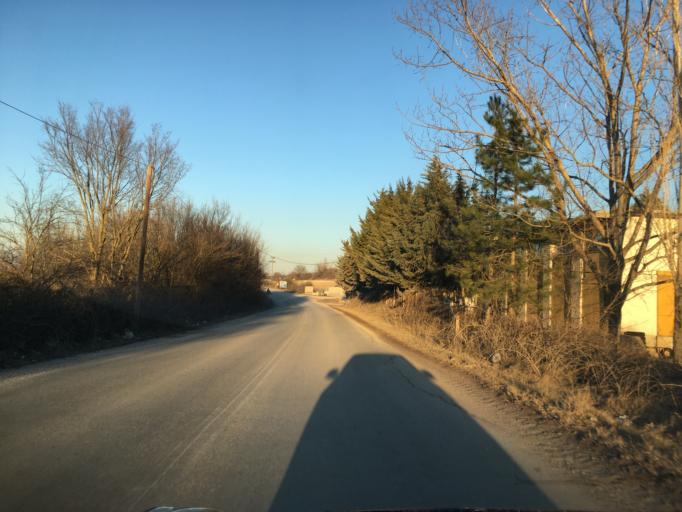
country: GR
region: West Macedonia
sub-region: Nomos Kozanis
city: Koila
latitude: 40.3246
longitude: 21.7838
